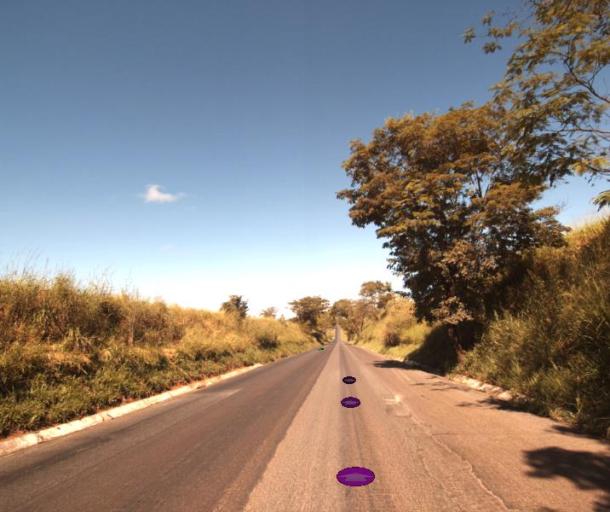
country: BR
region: Goias
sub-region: Itapaci
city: Itapaci
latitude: -15.1248
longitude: -49.5057
